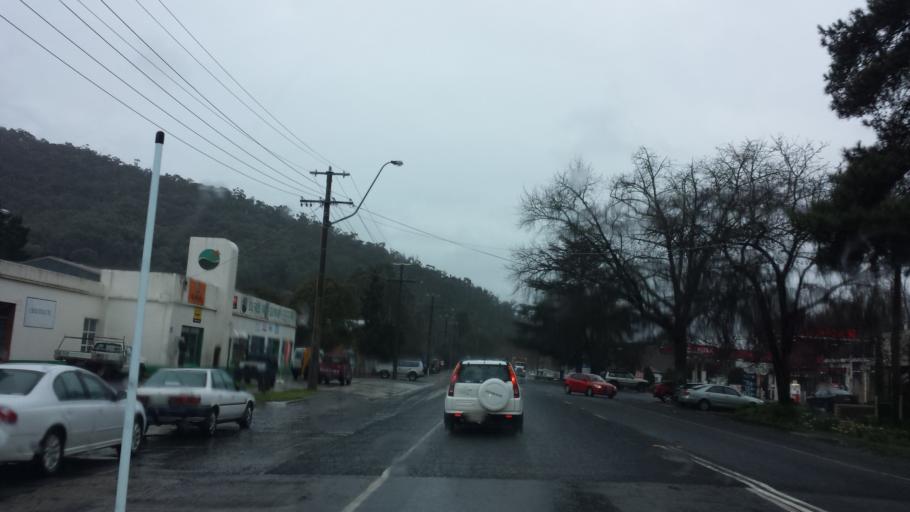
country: AU
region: Victoria
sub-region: Wangaratta
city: Wangaratta
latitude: -36.5638
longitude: 146.7280
